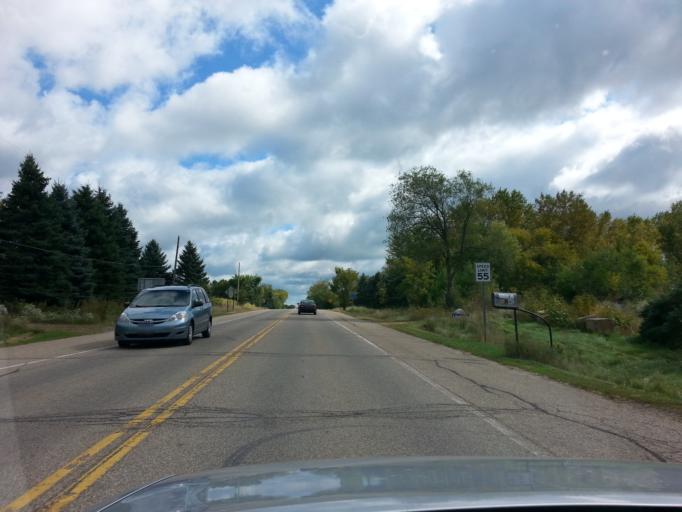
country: US
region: Minnesota
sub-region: Washington County
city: Lake Elmo
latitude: 44.9635
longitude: -92.9016
